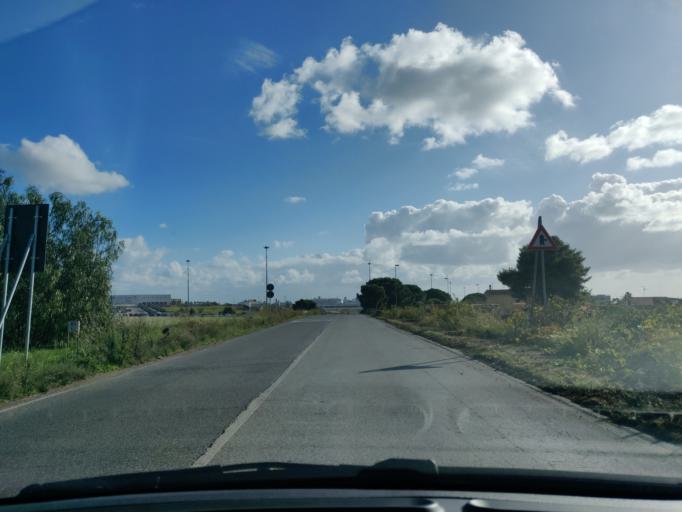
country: IT
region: Latium
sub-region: Citta metropolitana di Roma Capitale
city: Aurelia
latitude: 42.1290
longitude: 11.7731
